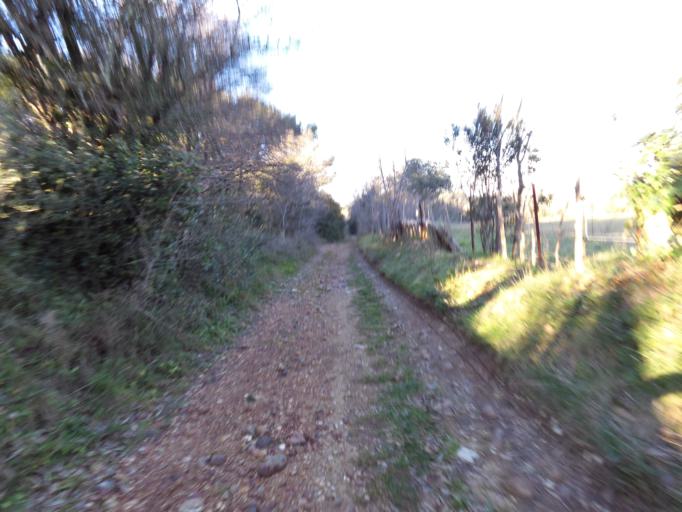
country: FR
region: Languedoc-Roussillon
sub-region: Departement du Gard
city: Aigues-Vives
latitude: 43.7273
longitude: 4.1759
